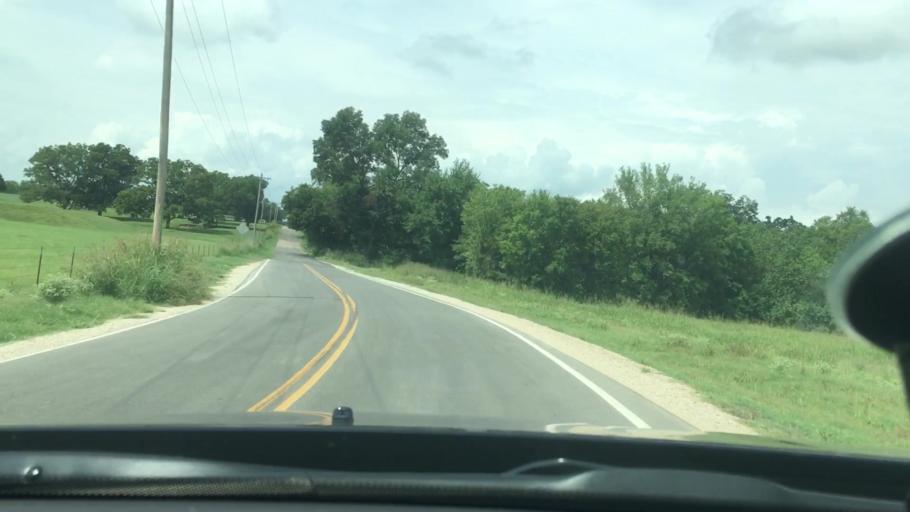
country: US
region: Oklahoma
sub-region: Carter County
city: Dickson
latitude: 34.2308
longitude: -96.9106
